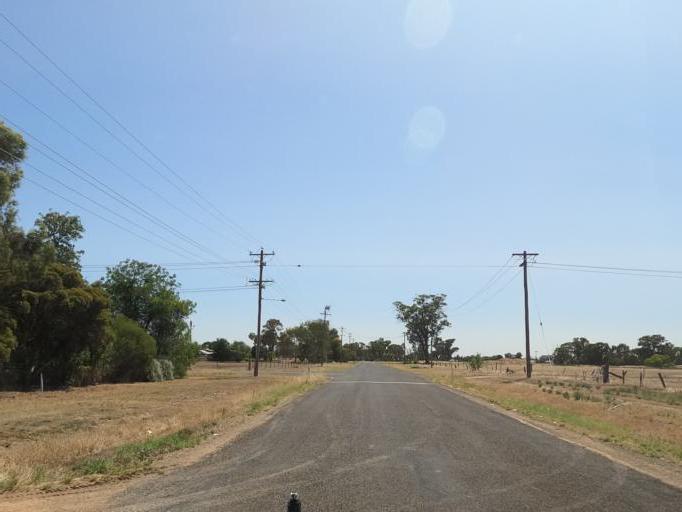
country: AU
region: New South Wales
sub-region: Corowa Shire
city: Mulwala
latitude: -35.9809
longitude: 146.0032
